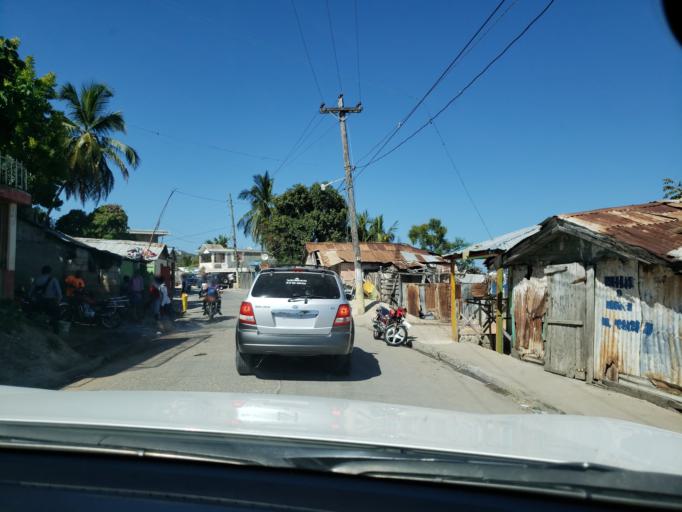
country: HT
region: Nippes
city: Miragoane
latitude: 18.4436
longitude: -73.0948
